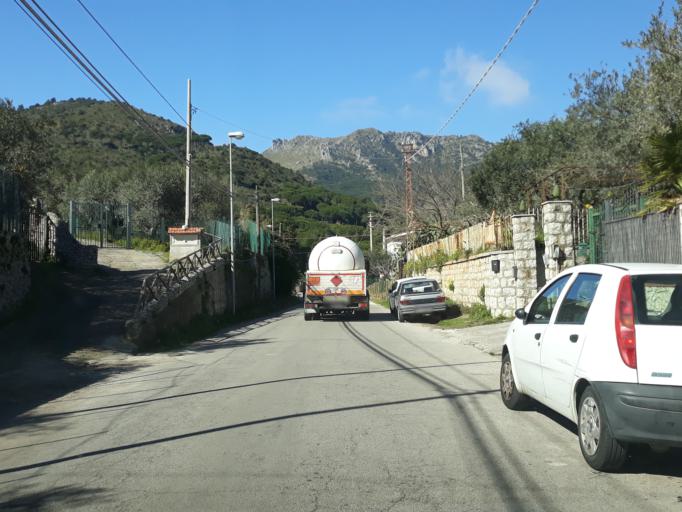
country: IT
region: Sicily
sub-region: Palermo
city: Piano dei Geli
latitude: 38.0856
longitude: 13.2617
